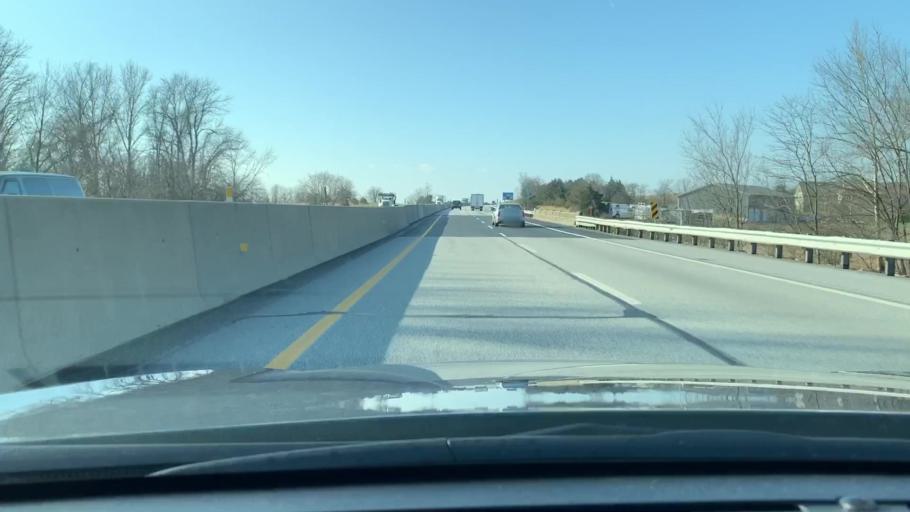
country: US
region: Pennsylvania
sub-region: Lancaster County
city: Elizabethtown
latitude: 40.2084
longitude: -76.5616
